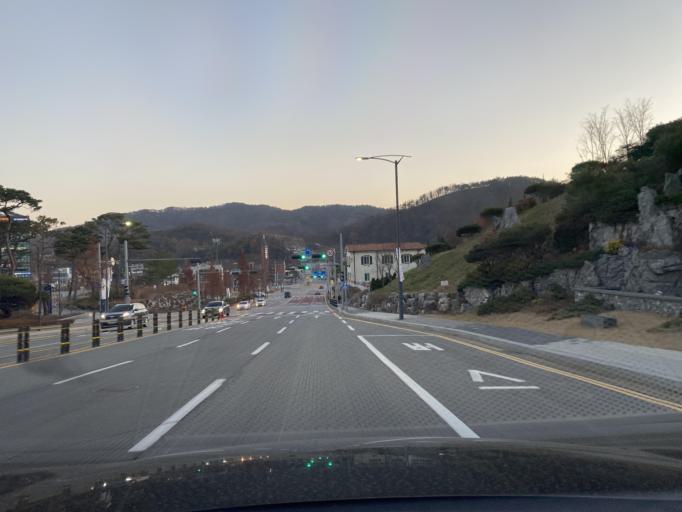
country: KR
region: Chungcheongnam-do
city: Yesan
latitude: 36.6810
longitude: 126.8434
